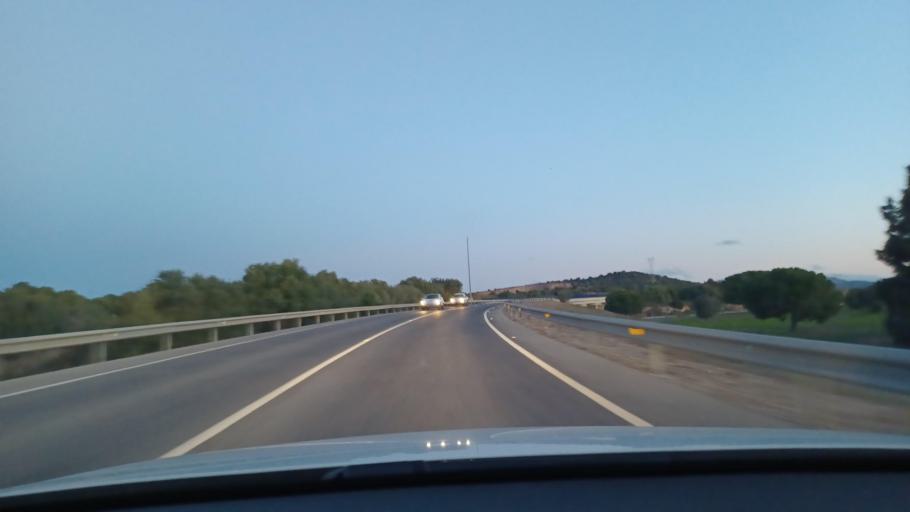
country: ES
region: Catalonia
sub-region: Provincia de Tarragona
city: Amposta
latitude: 40.7304
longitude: 0.5852
